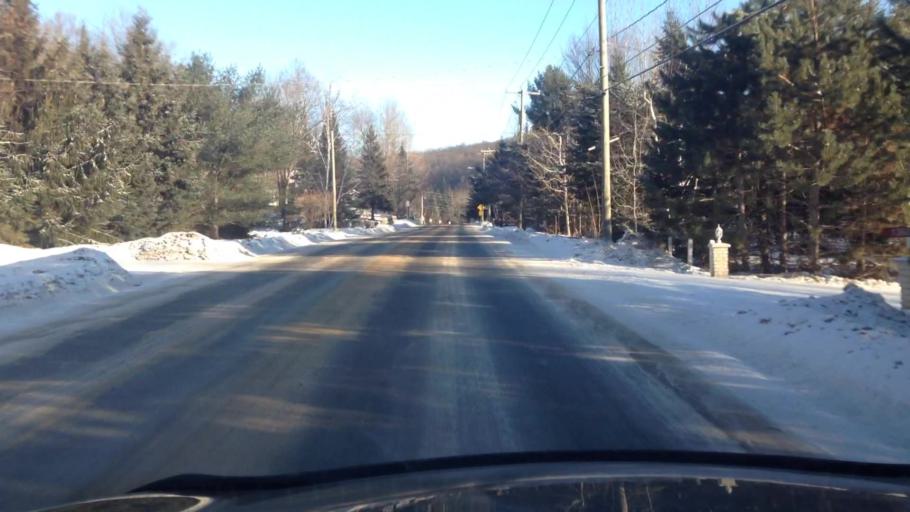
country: CA
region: Quebec
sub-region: Laurentides
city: Sainte-Agathe-des-Monts
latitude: 45.9289
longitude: -74.4649
